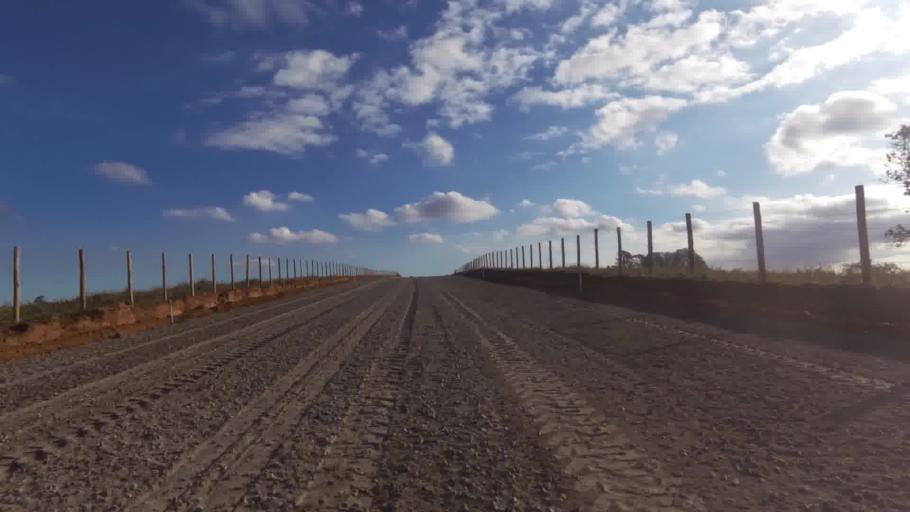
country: BR
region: Espirito Santo
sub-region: Marataizes
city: Marataizes
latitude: -21.1094
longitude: -41.0455
